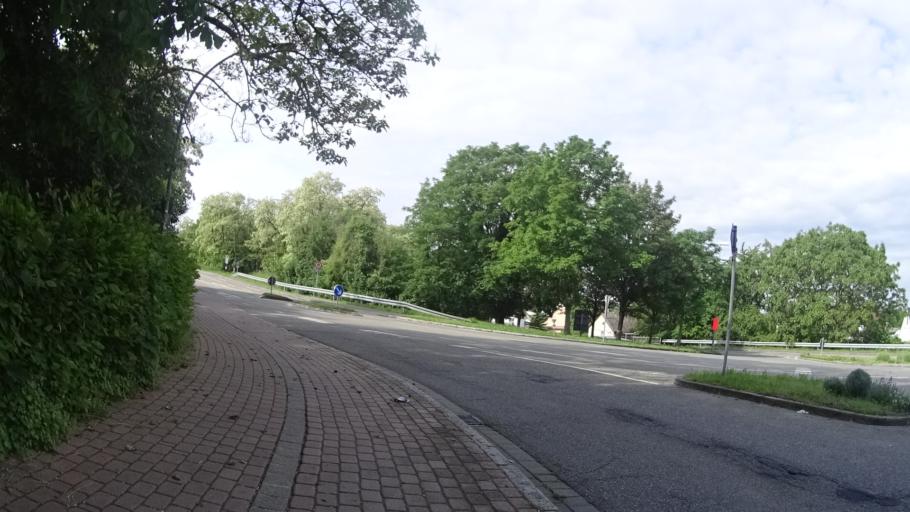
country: DE
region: Baden-Wuerttemberg
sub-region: Freiburg Region
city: Neuenburg am Rhein
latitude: 47.8093
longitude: 7.5637
